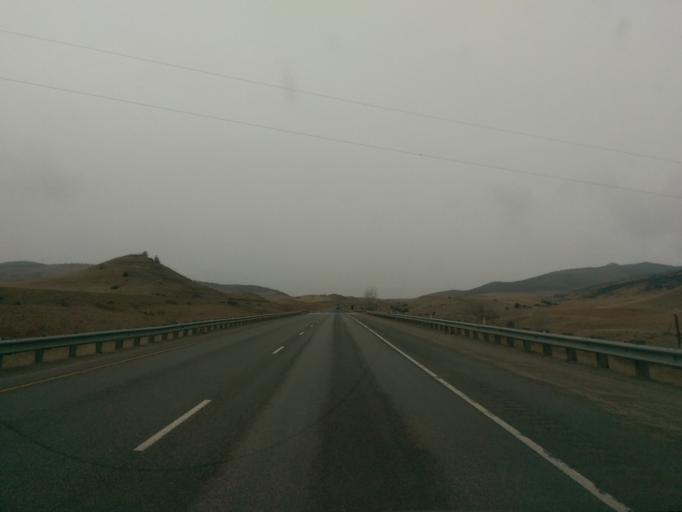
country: US
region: Montana
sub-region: Gallatin County
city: Three Forks
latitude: 45.9021
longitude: -111.8130
